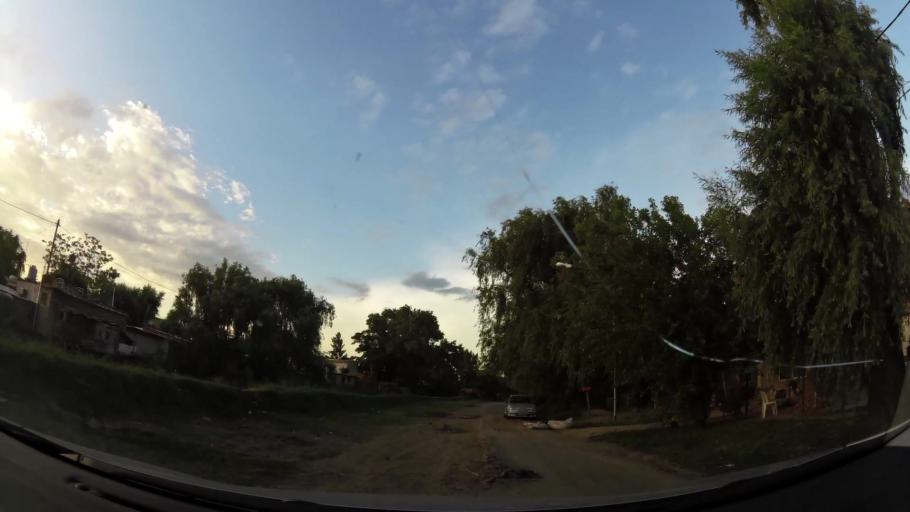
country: AR
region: Buenos Aires
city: Santa Catalina - Dique Lujan
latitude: -34.4471
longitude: -58.6666
